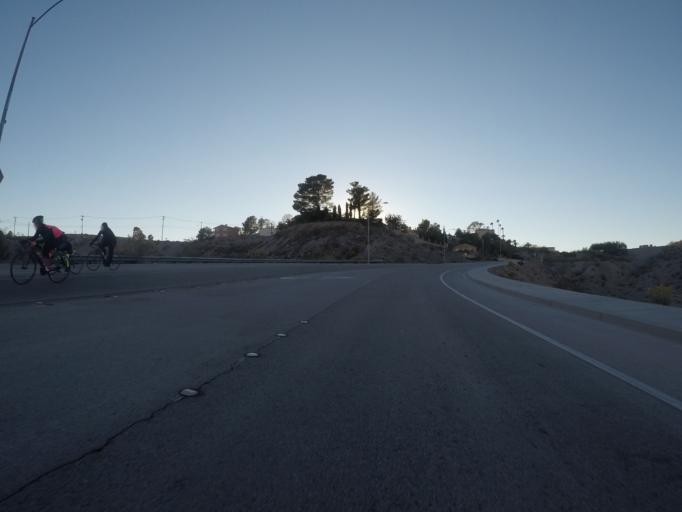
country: US
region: Nevada
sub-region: Clark County
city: Boulder City
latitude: 35.9815
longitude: -114.8299
